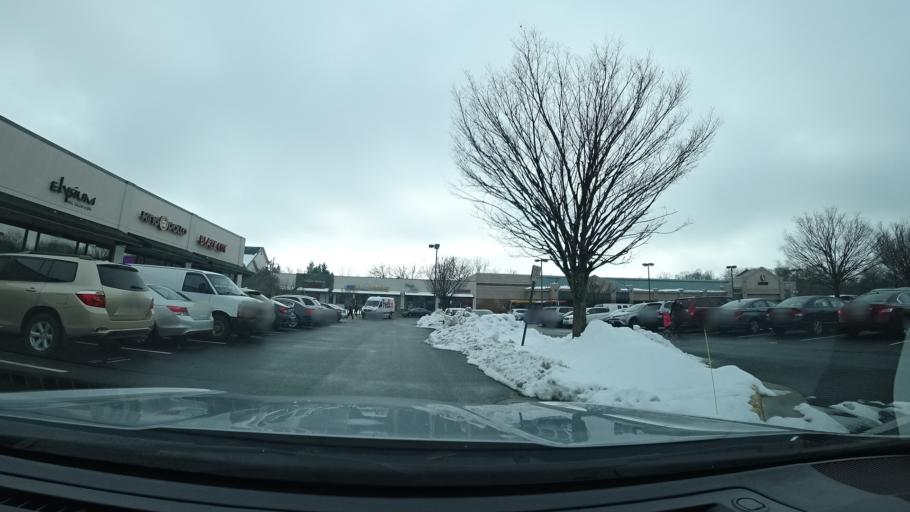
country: US
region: Virginia
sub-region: Fairfax County
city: Reston
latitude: 38.9366
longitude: -77.3619
